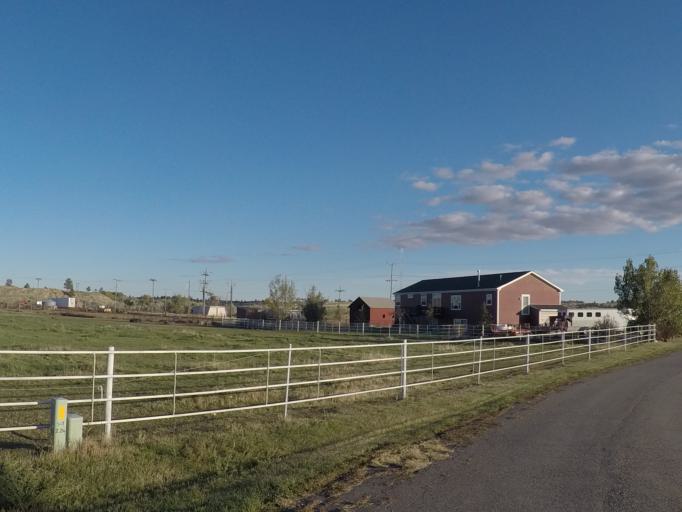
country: US
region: Montana
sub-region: Golden Valley County
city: Ryegate
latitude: 46.2935
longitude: -108.9336
